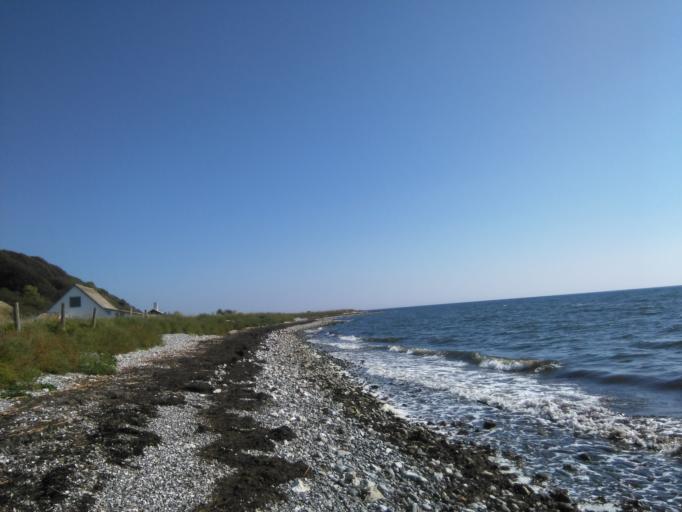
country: DK
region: Central Jutland
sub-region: Syddjurs Kommune
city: Ebeltoft
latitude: 56.2435
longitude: 10.7796
